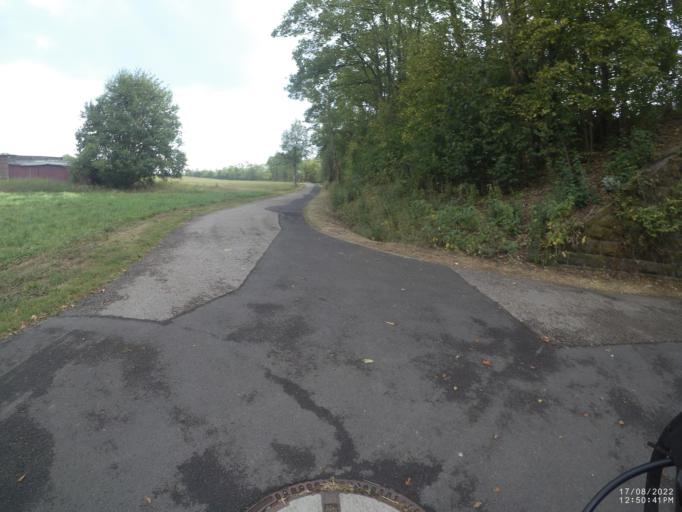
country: DE
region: Rheinland-Pfalz
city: Hillesheim
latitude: 50.2907
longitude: 6.6758
